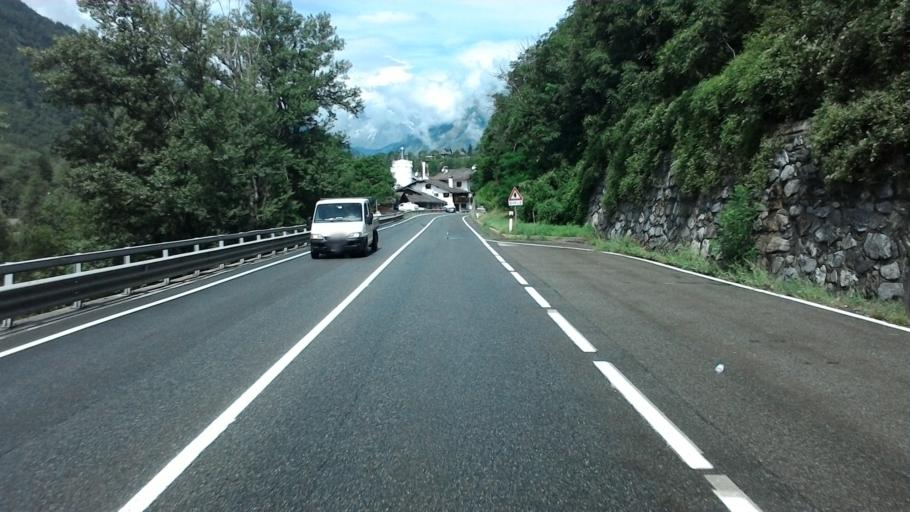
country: IT
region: Aosta Valley
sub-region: Valle d'Aosta
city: La Salle
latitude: 45.7271
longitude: 7.0918
